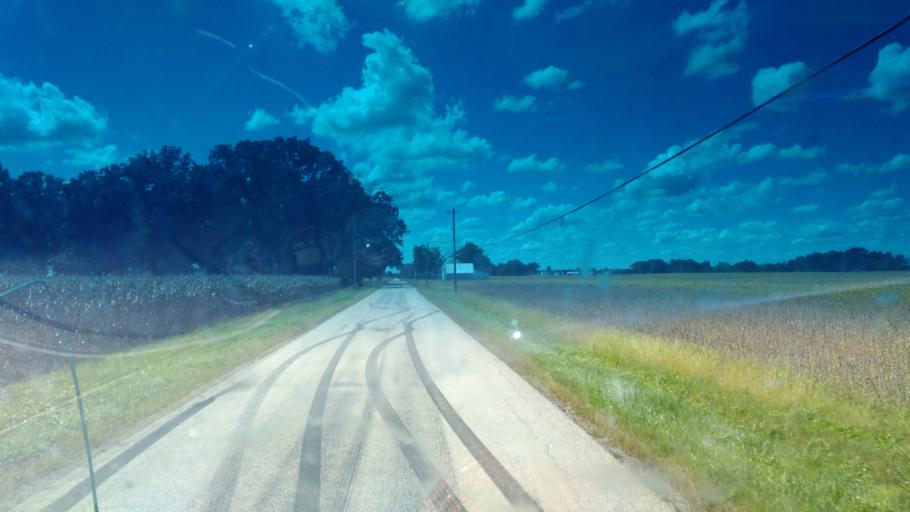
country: US
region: Ohio
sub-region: Madison County
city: West Jefferson
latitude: 39.9864
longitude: -83.3162
